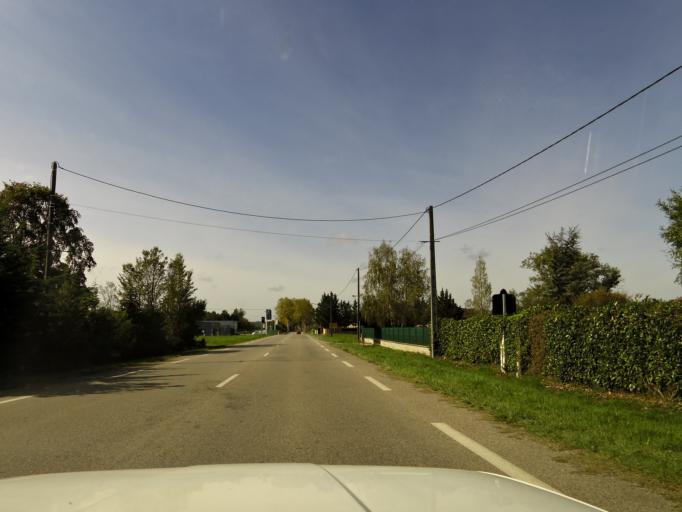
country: FR
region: Rhone-Alpes
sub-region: Departement de l'Ain
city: Chazey-sur-Ain
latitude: 45.9066
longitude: 5.2275
